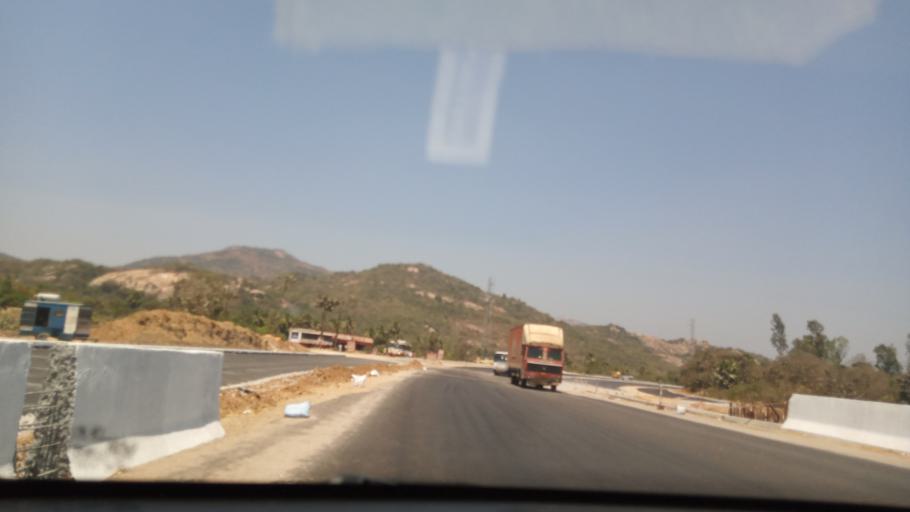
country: IN
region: Andhra Pradesh
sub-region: Chittoor
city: Pakala
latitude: 13.4711
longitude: 79.1801
